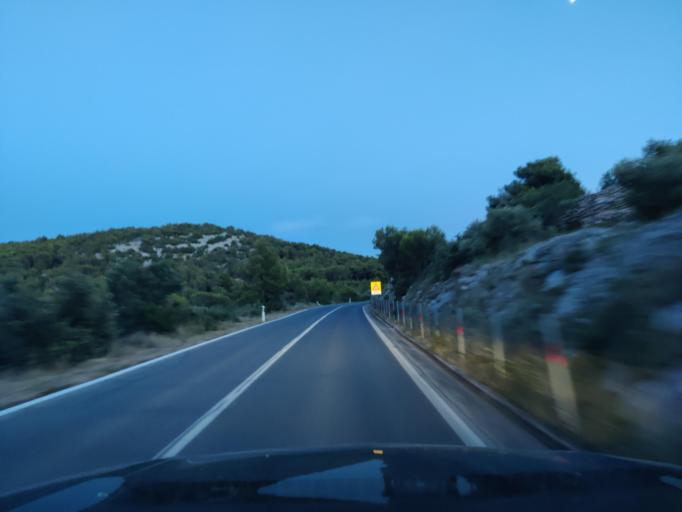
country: HR
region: Sibensko-Kniniska
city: Murter
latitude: 43.8034
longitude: 15.6106
